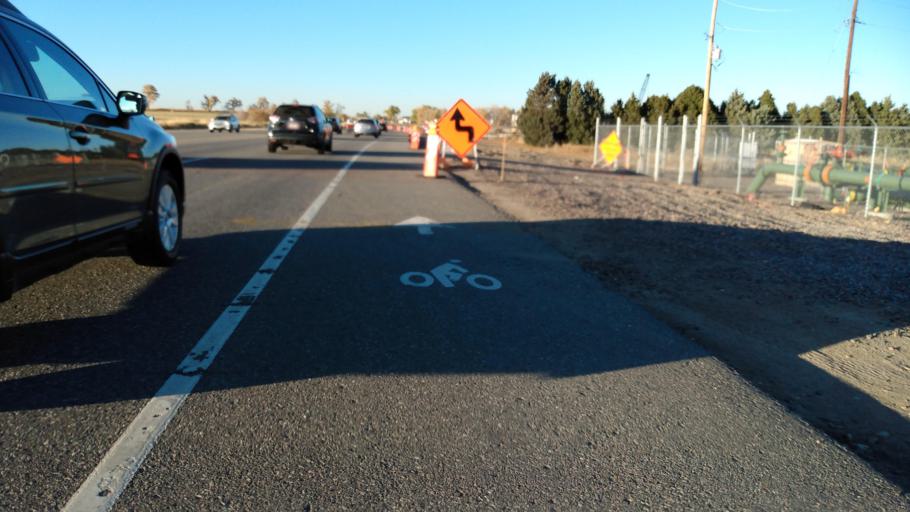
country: US
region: Colorado
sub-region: Boulder County
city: Louisville
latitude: 39.9584
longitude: -105.1275
